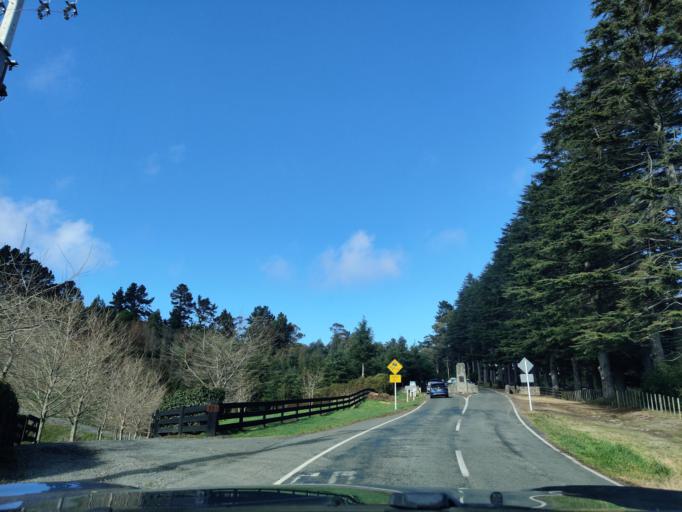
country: NZ
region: Hawke's Bay
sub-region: Hastings District
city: Hastings
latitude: -39.6938
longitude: 176.9022
